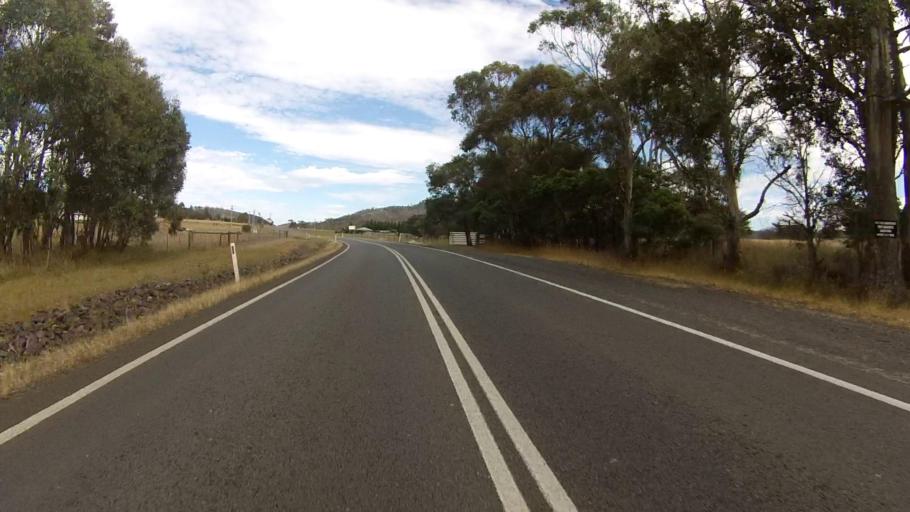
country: AU
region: Tasmania
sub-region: Brighton
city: Old Beach
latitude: -42.6705
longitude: 147.3893
